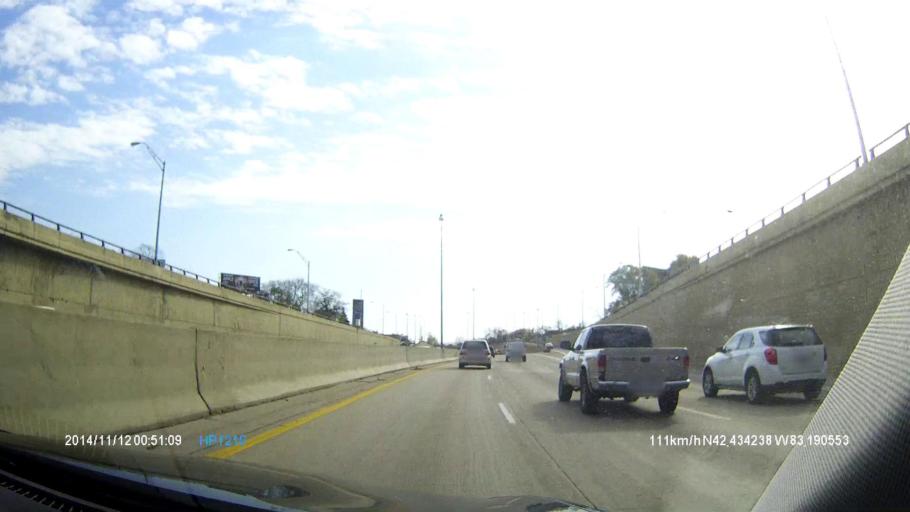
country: US
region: Michigan
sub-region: Oakland County
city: Oak Park
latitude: 42.4338
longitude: -83.1901
